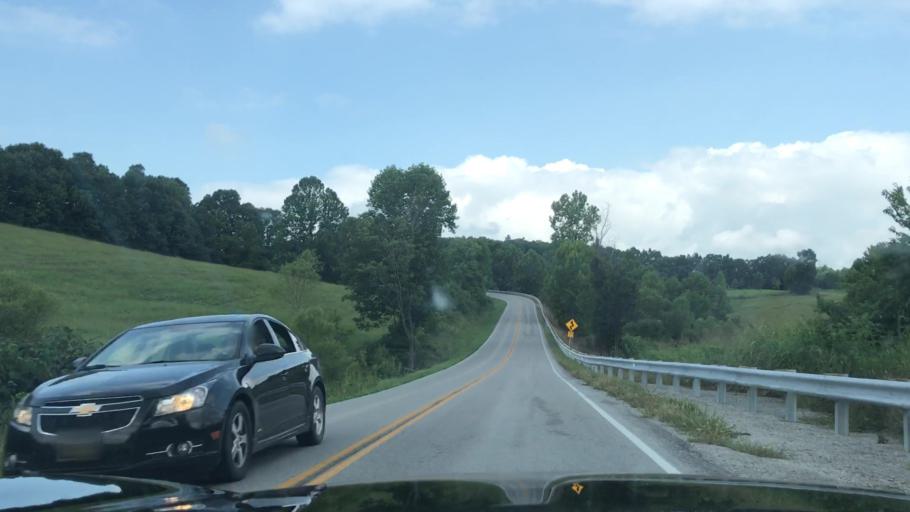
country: US
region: Kentucky
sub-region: Butler County
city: Morgantown
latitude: 37.1787
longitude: -86.8538
